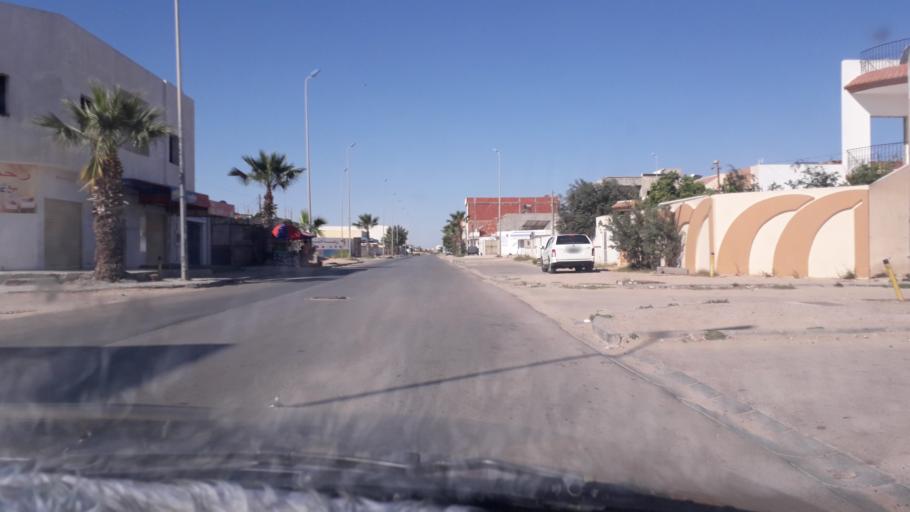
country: TN
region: Safaqis
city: Al Qarmadah
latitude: 34.8263
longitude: 10.7503
